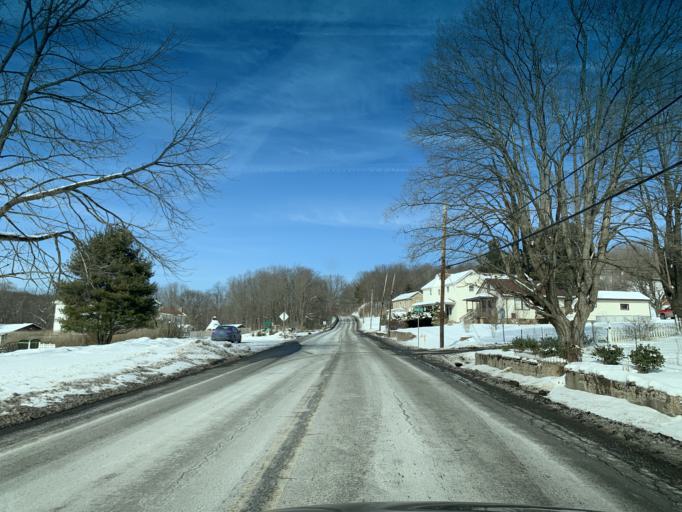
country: US
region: Maryland
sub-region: Allegany County
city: Frostburg
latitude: 39.6279
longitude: -78.9364
